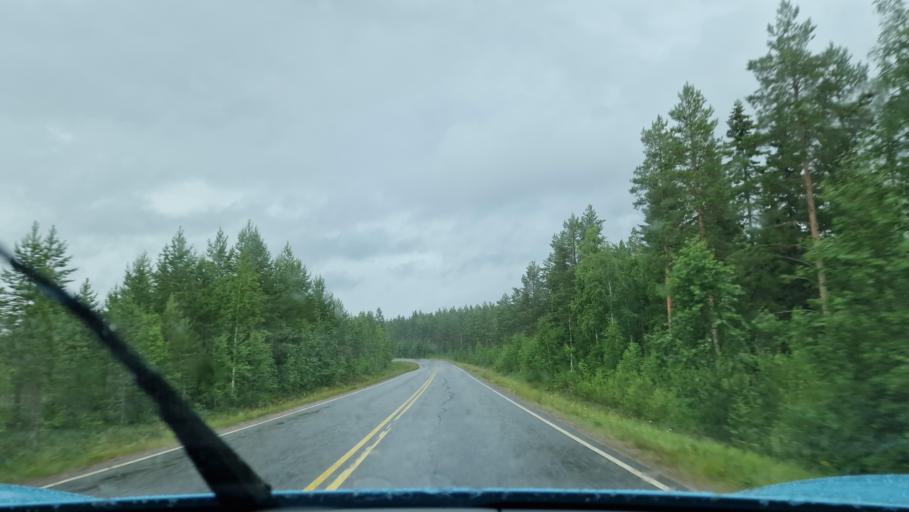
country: FI
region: Southern Ostrobothnia
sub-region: Jaerviseutu
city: Soini
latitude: 62.8107
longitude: 24.3603
